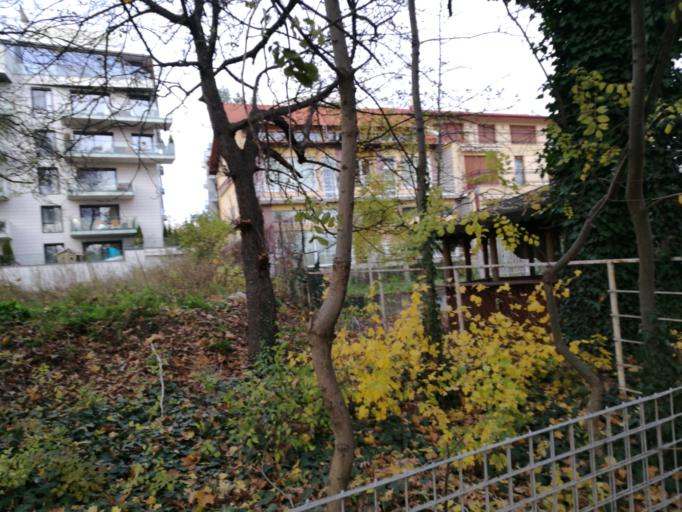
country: RO
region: Bucuresti
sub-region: Municipiul Bucuresti
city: Bucharest
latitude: 44.4764
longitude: 26.0954
